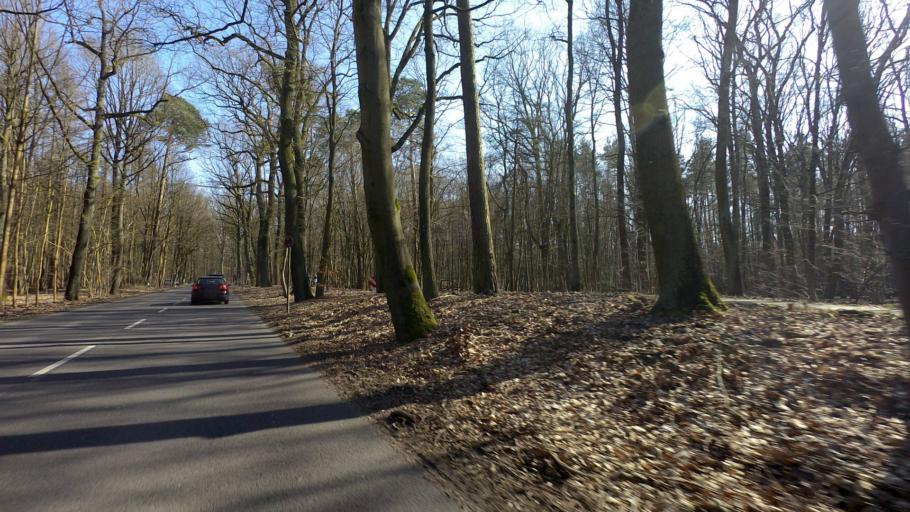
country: DE
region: Berlin
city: Konradshohe
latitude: 52.5852
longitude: 13.2060
